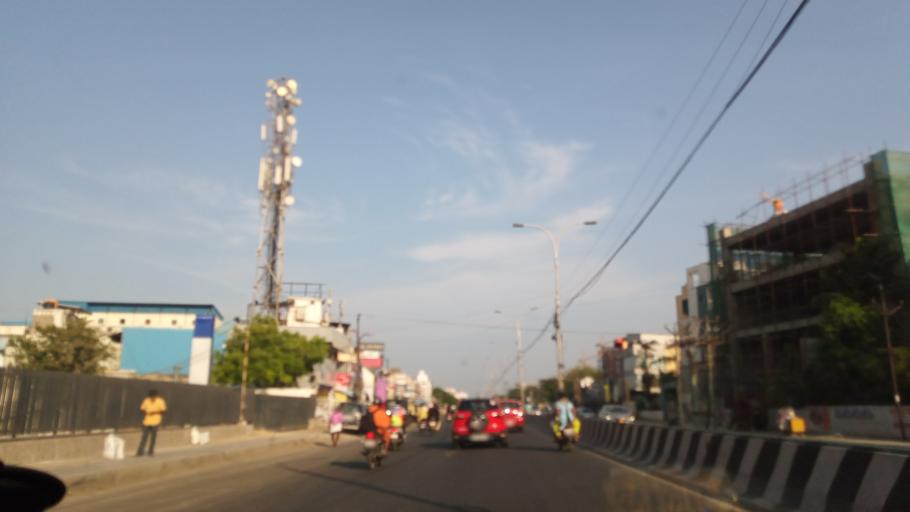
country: IN
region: Tamil Nadu
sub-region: Thiruvallur
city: Porur
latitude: 13.0292
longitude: 80.1691
